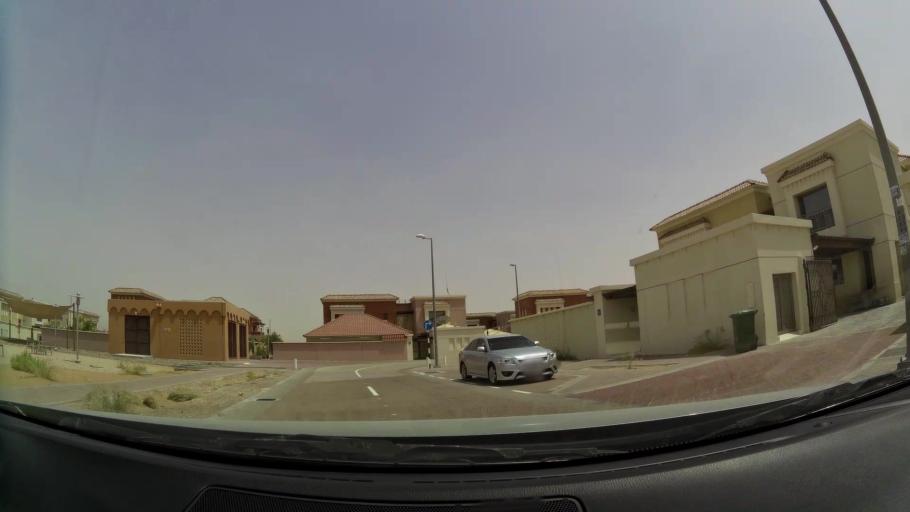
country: AE
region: Abu Dhabi
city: Al Ain
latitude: 24.1502
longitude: 55.6313
